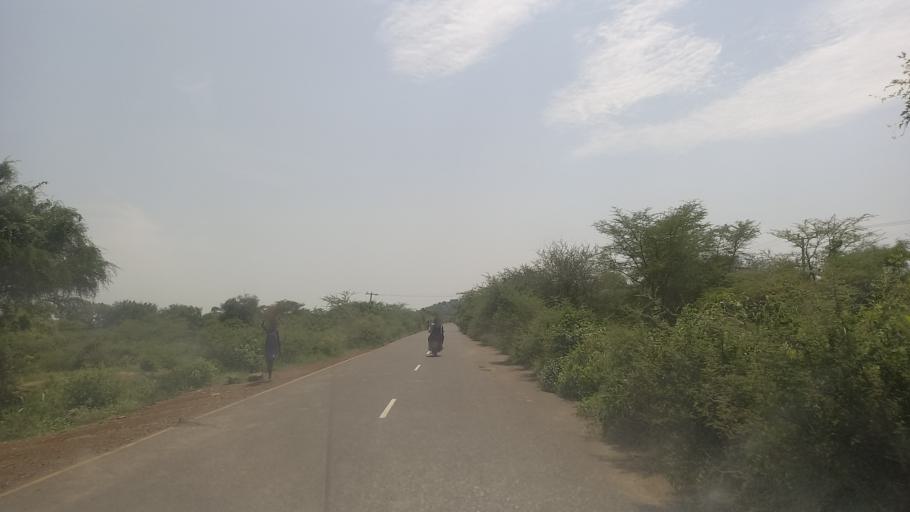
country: ET
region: Gambela
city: Gambela
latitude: 8.2805
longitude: 34.2247
